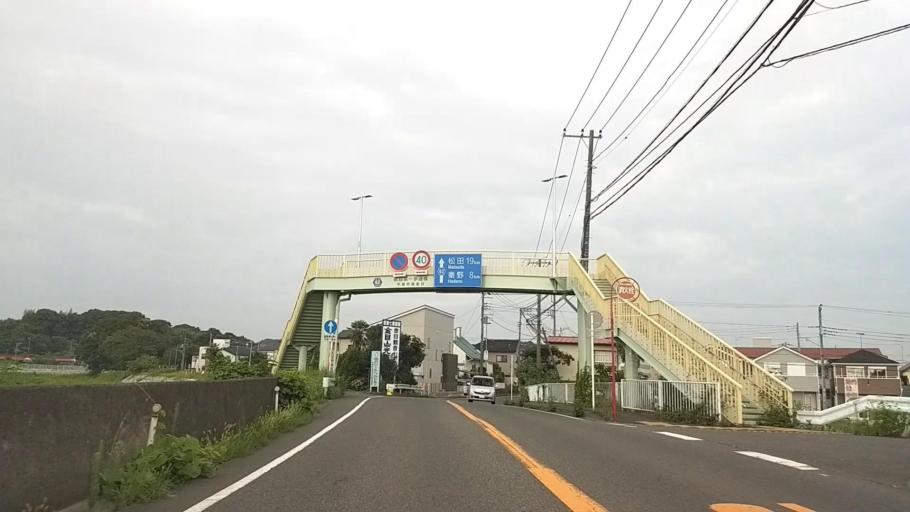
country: JP
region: Kanagawa
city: Isehara
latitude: 35.3594
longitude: 139.2939
